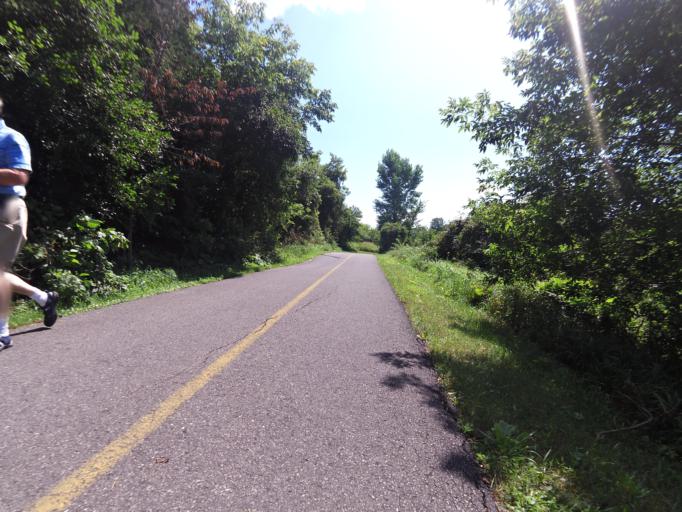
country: CA
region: Ontario
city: Ottawa
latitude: 45.3626
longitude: -75.6637
